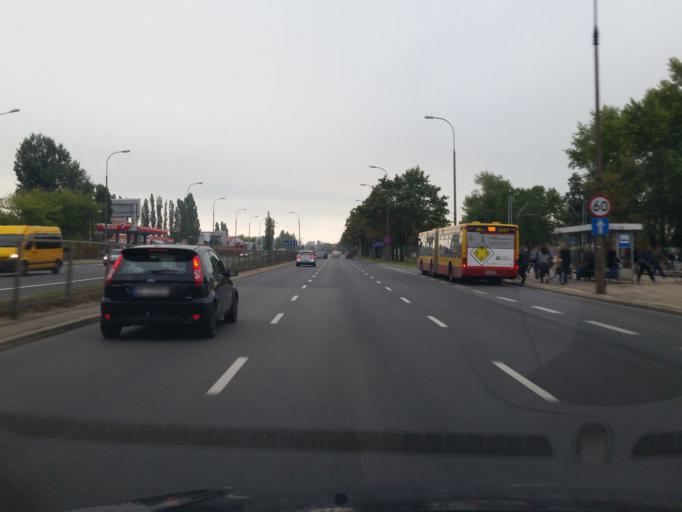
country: PL
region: Masovian Voivodeship
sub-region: Warszawa
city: Zoliborz
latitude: 52.2787
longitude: 21.0118
